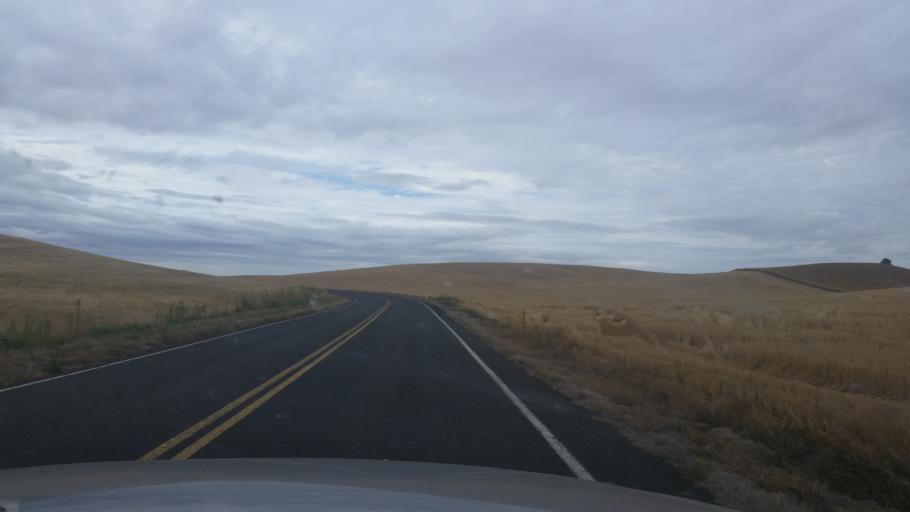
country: US
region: Washington
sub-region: Spokane County
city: Medical Lake
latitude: 47.5279
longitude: -117.8542
